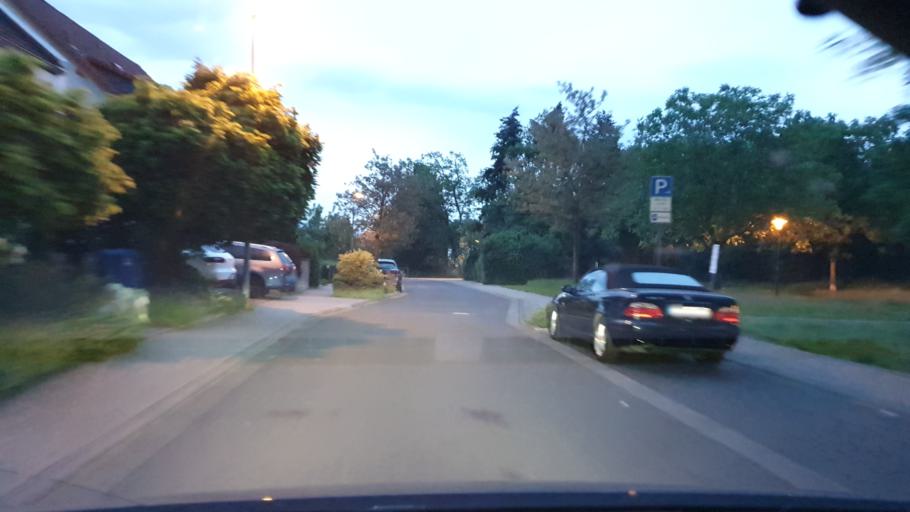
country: DE
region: Hesse
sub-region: Regierungsbezirk Darmstadt
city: Hofheim am Taunus
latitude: 50.0806
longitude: 8.4465
